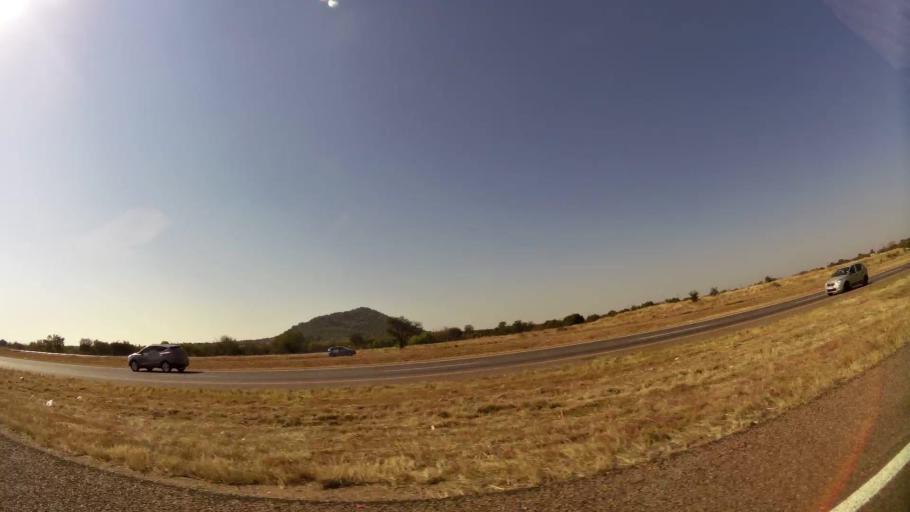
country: ZA
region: North-West
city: Ga-Rankuwa
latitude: -25.6257
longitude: 28.1107
